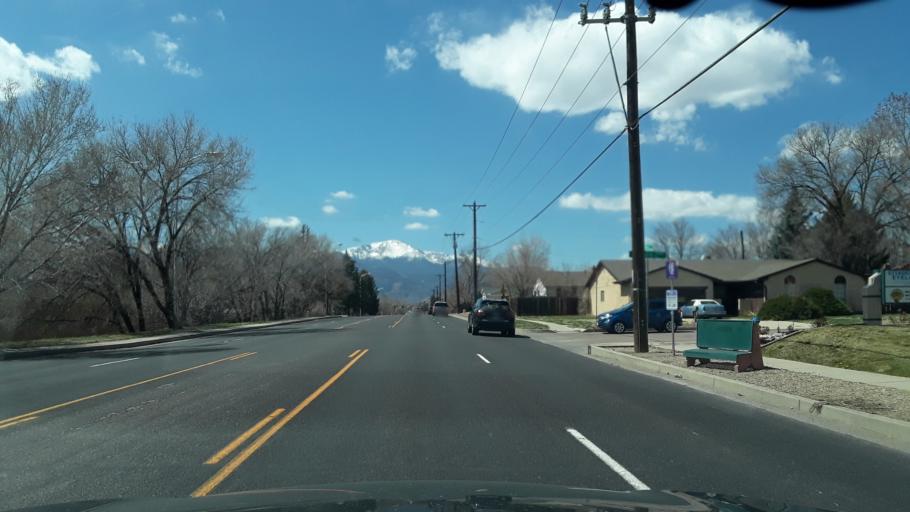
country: US
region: Colorado
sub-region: El Paso County
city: Colorado Springs
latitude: 38.8471
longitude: -104.7631
